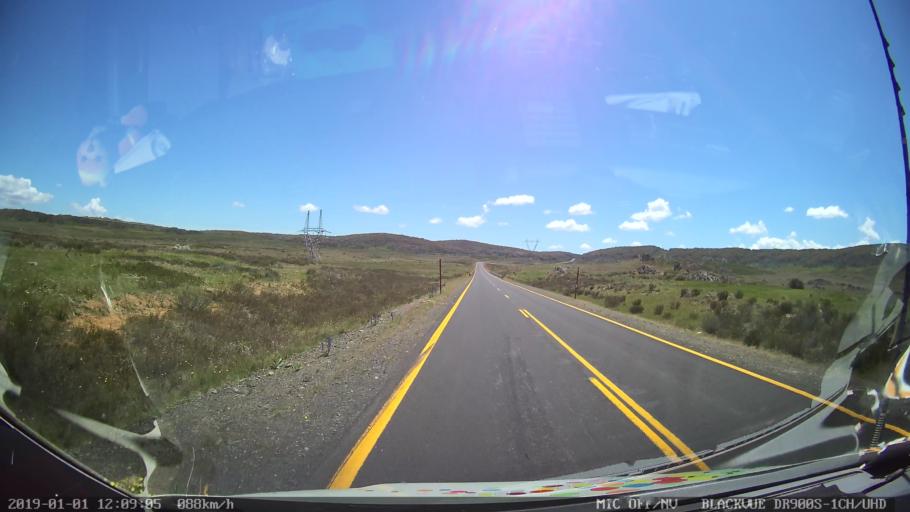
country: AU
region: New South Wales
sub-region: Tumut Shire
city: Tumut
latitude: -35.8119
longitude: 148.4962
